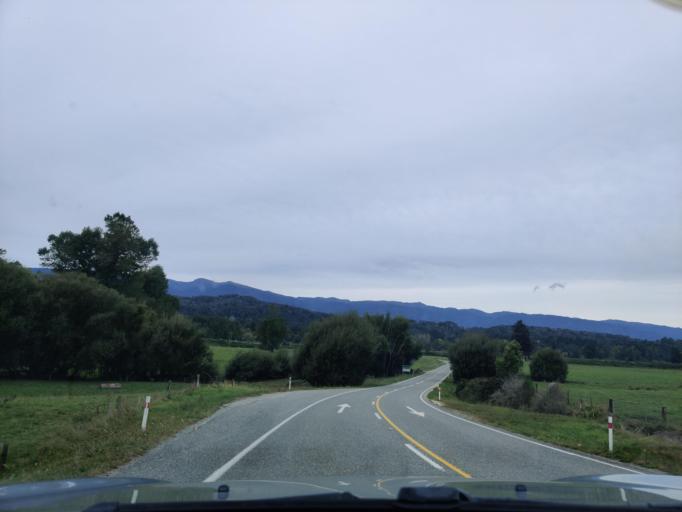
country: NZ
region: West Coast
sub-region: Buller District
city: Westport
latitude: -41.8580
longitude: 171.9375
